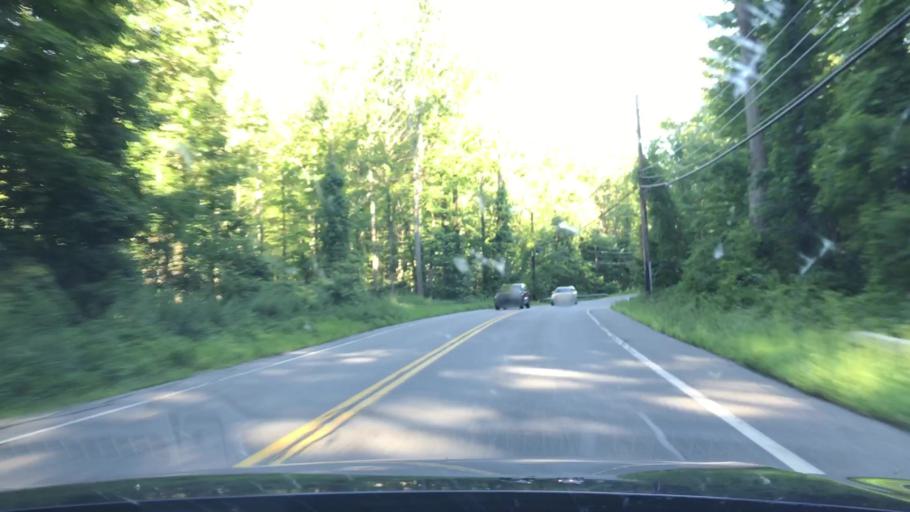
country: US
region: New York
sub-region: Putnam County
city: Mahopac
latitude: 41.3767
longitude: -73.7070
